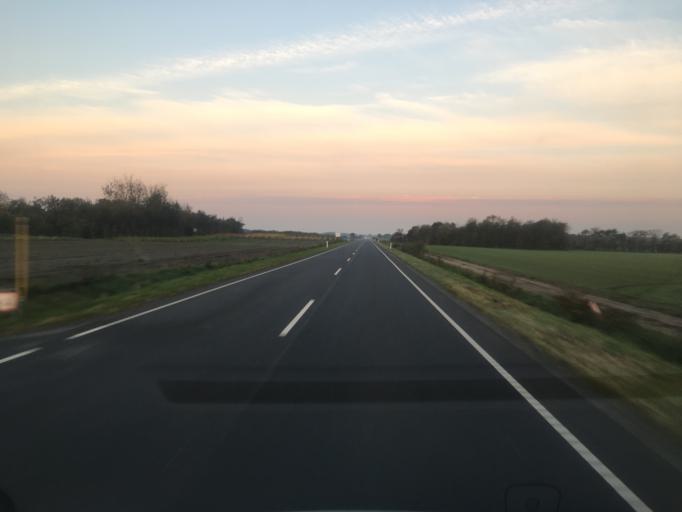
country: DE
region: Schleswig-Holstein
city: Bramstedtlund
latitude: 54.9717
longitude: 9.0815
